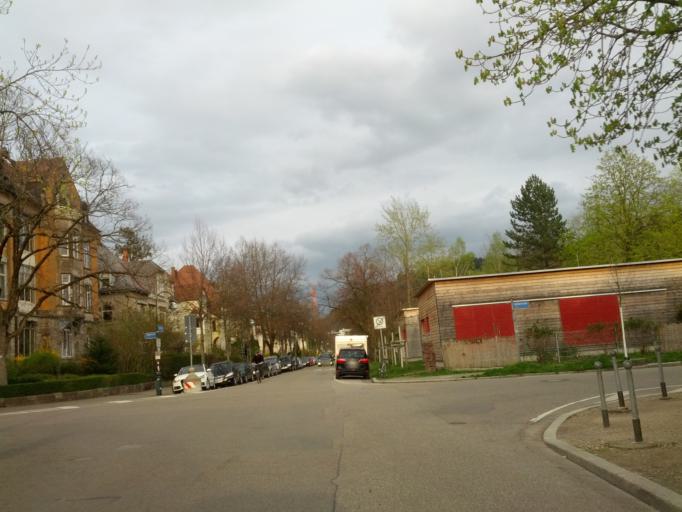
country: DE
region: Baden-Wuerttemberg
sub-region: Freiburg Region
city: Freiburg
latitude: 47.9850
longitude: 7.8535
